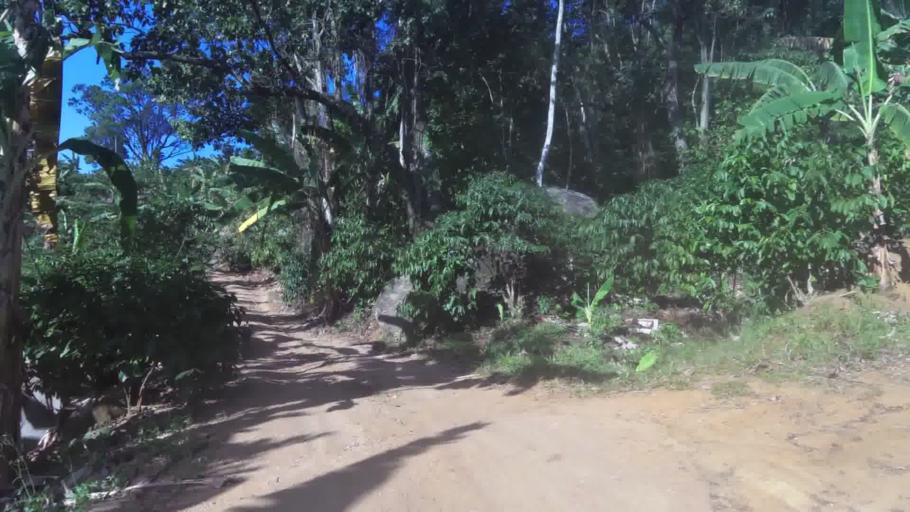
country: BR
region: Espirito Santo
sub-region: Iconha
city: Iconha
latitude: -20.7548
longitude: -40.8097
